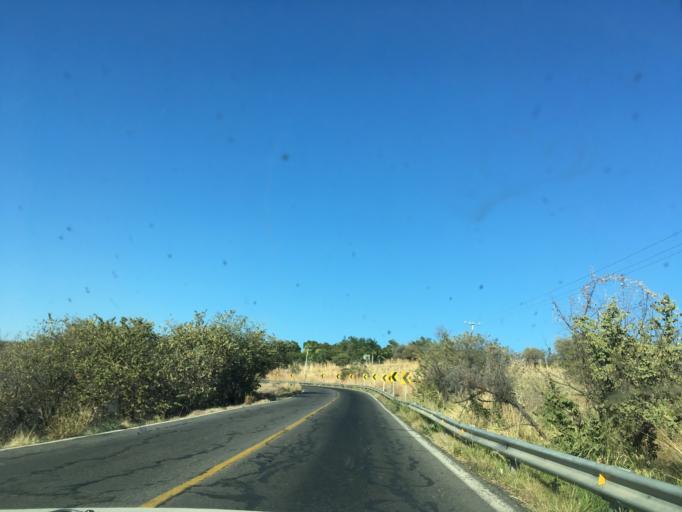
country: MX
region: Michoacan
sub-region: Gabriel Zamora
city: Lombardia
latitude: 19.1971
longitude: -102.0552
